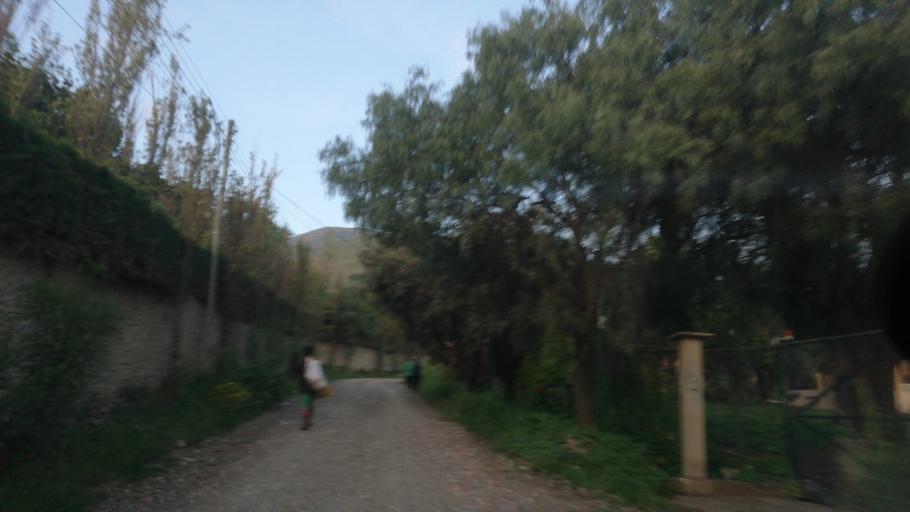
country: BO
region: Cochabamba
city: Cochabamba
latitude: -17.3345
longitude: -66.2092
